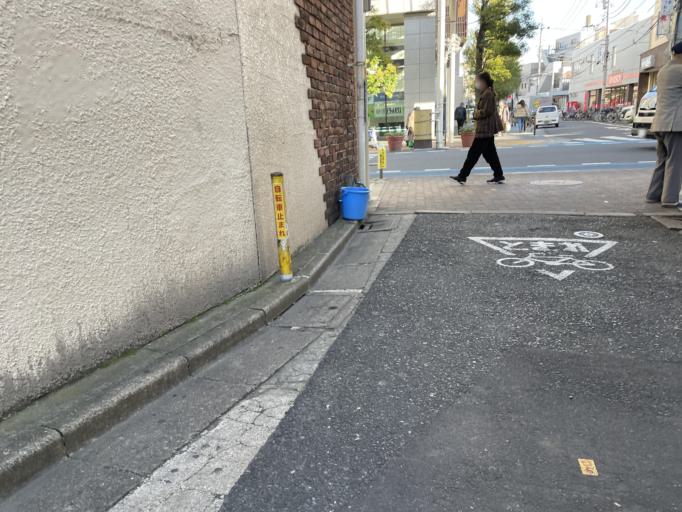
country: JP
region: Chiba
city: Matsudo
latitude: 35.7314
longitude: 139.8814
